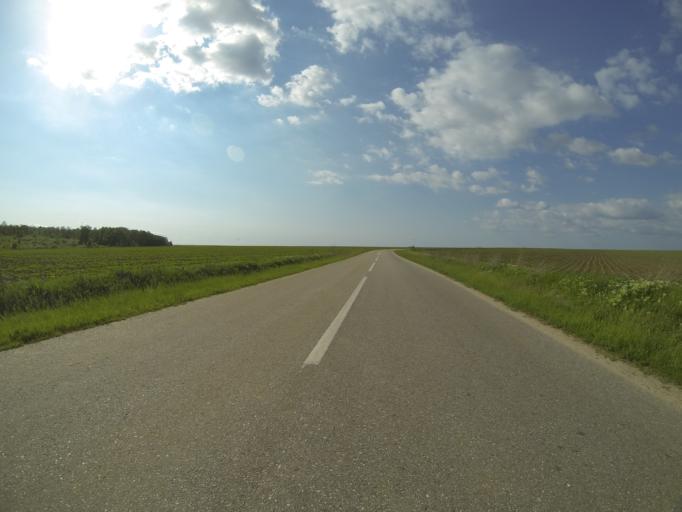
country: RO
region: Dolj
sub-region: Comuna Plenita
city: Castrele Traiane
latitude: 44.2546
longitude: 23.1508
